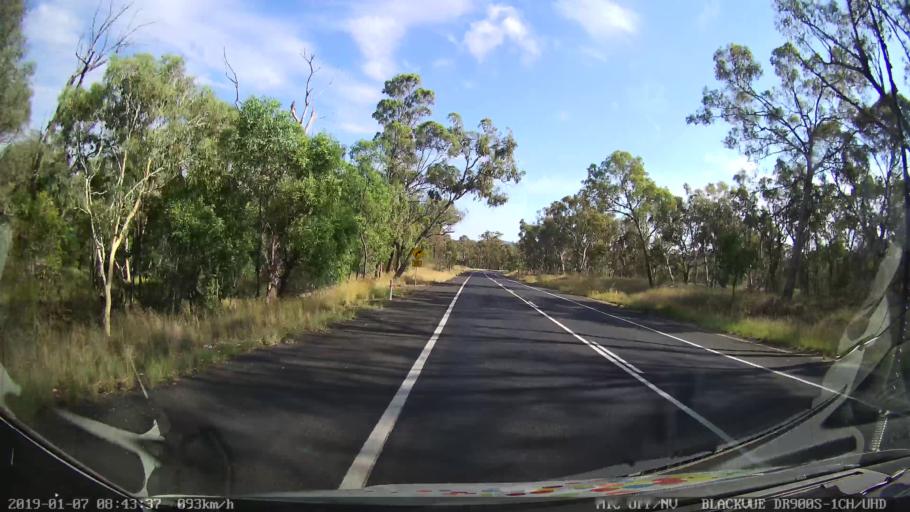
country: AU
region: New South Wales
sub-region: Tamworth Municipality
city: Kootingal
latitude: -30.8424
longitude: 151.2154
